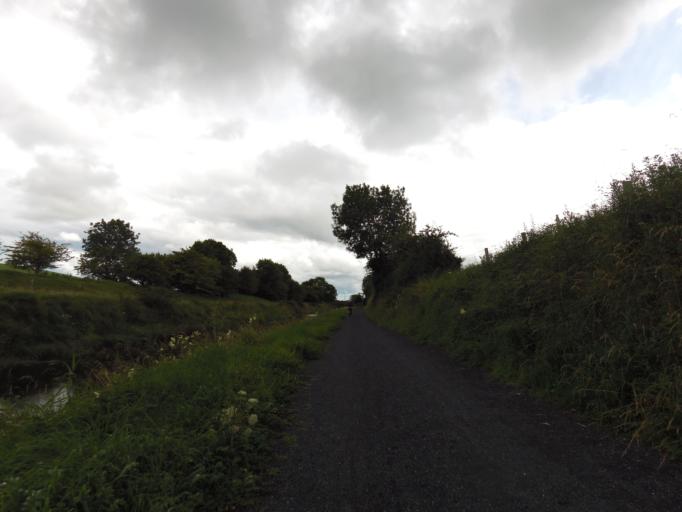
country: IE
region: Leinster
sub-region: An Iarmhi
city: An Muileann gCearr
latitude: 53.5261
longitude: -7.4476
